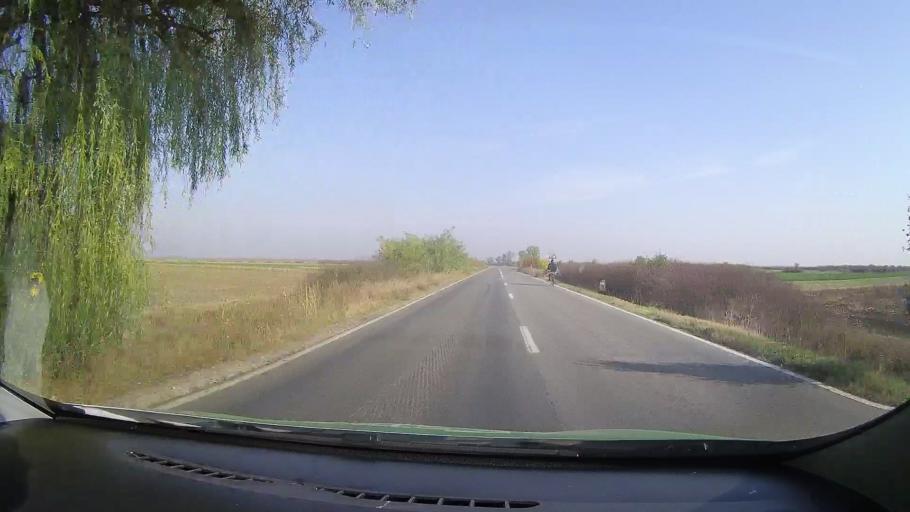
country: RO
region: Arad
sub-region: Comuna Pilu
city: Pilu
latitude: 46.5950
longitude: 21.3478
